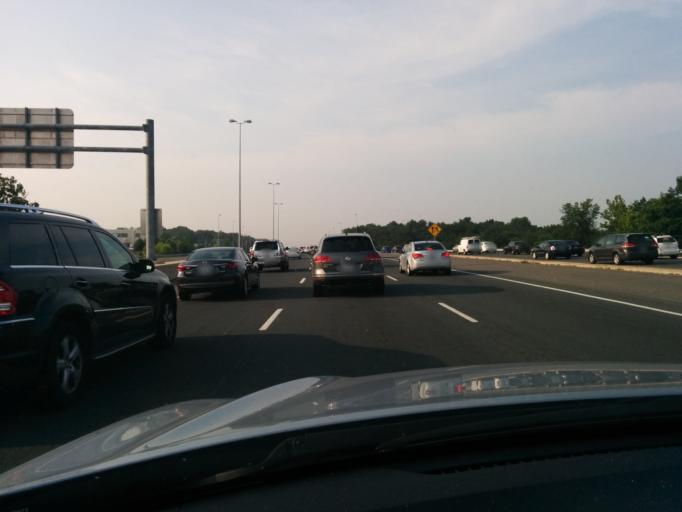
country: US
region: Virginia
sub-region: Loudoun County
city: Sterling
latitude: 38.9998
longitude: -77.4350
